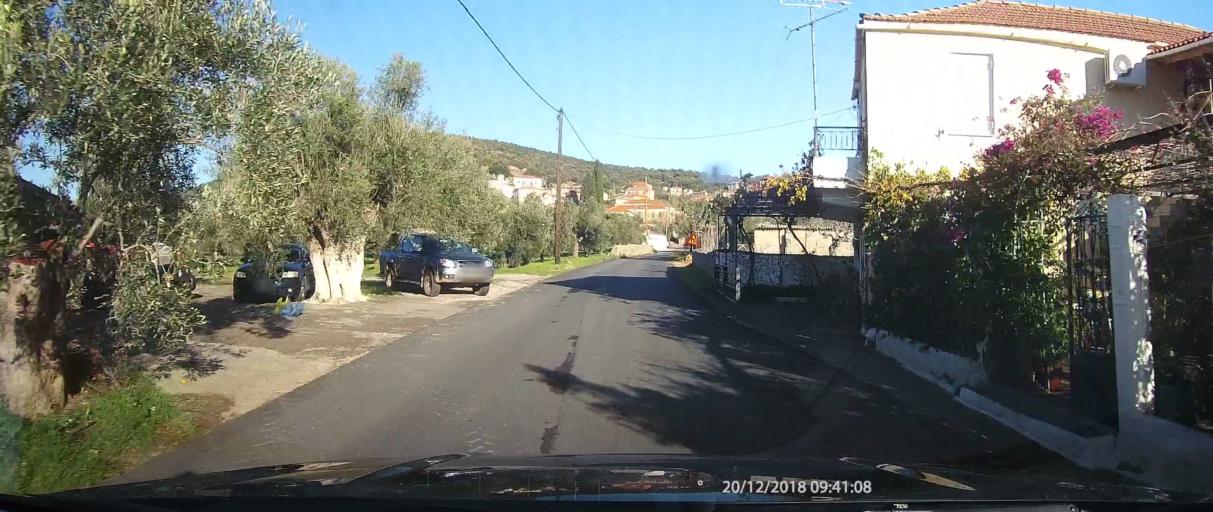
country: GR
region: Peloponnese
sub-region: Nomos Lakonias
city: Yerakion
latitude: 36.9513
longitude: 22.7659
